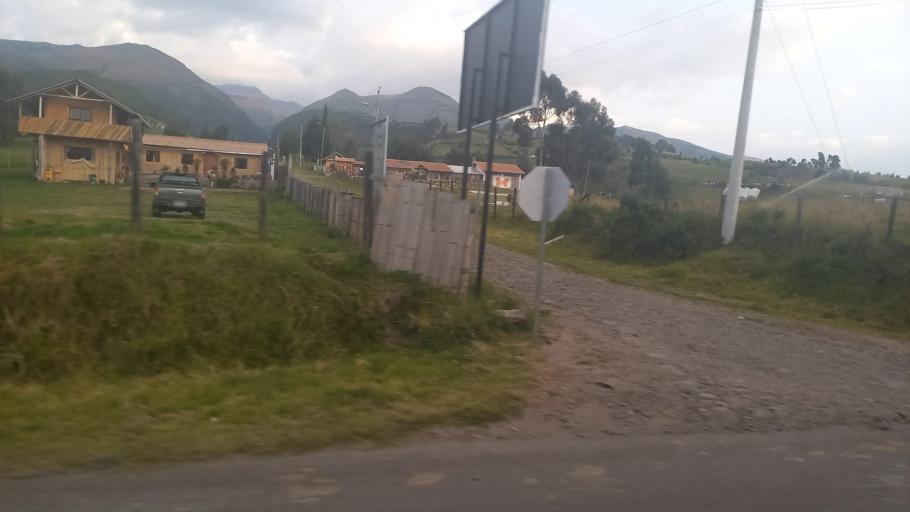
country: EC
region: Pichincha
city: Cayambe
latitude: 0.0929
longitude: -78.0912
